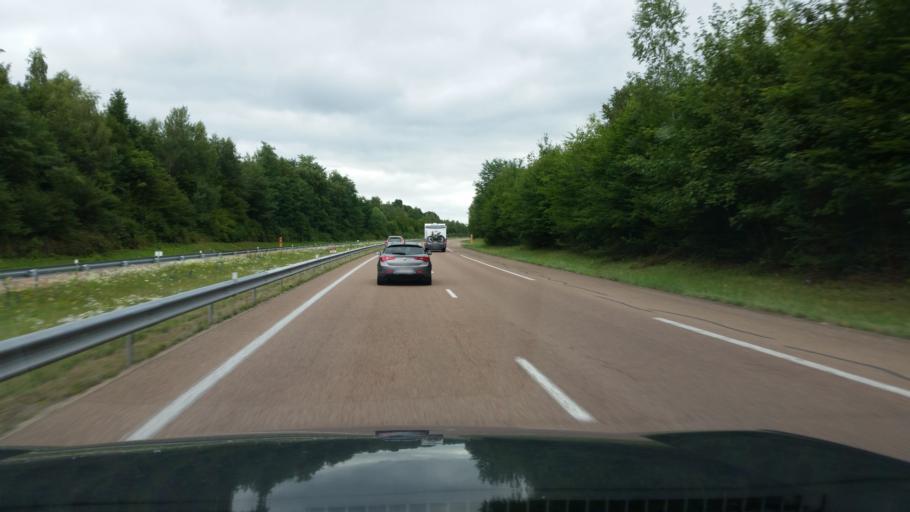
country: FR
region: Franche-Comte
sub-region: Departement du Jura
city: Bletterans
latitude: 46.7115
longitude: 5.4858
